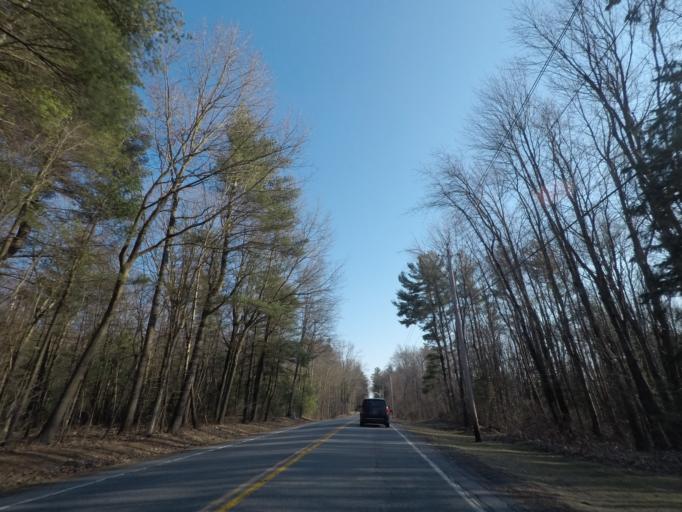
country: US
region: New York
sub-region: Schenectady County
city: Niskayuna
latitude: 42.8286
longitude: -73.7756
